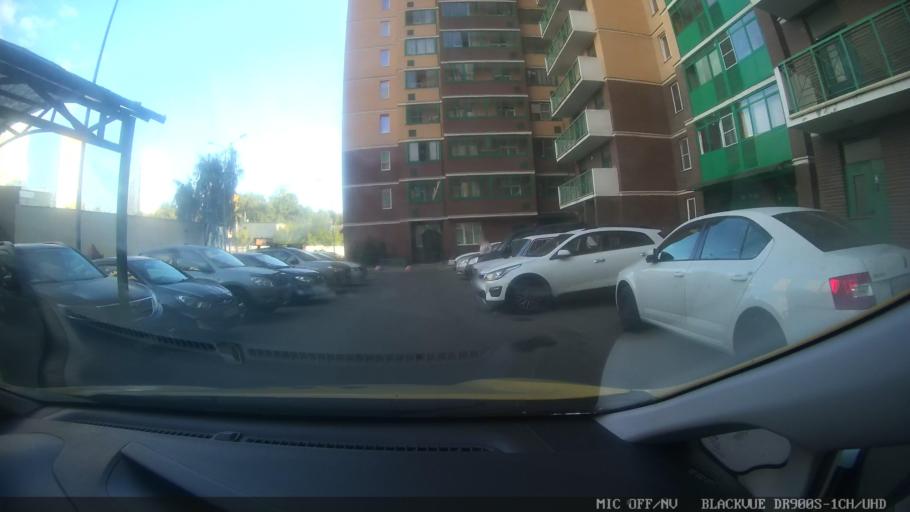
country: RU
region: Moscow
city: Zagor'ye
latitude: 55.5776
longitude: 37.6752
